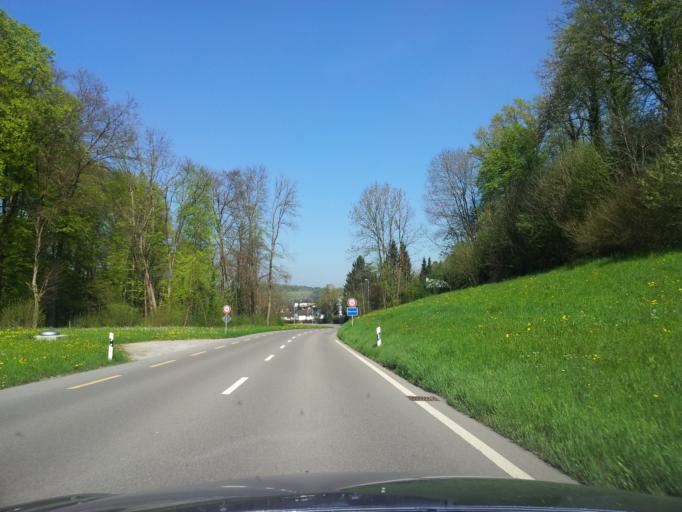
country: CH
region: Zurich
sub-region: Bezirk Dietikon
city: Birmensdorf
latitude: 47.3463
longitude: 8.4453
